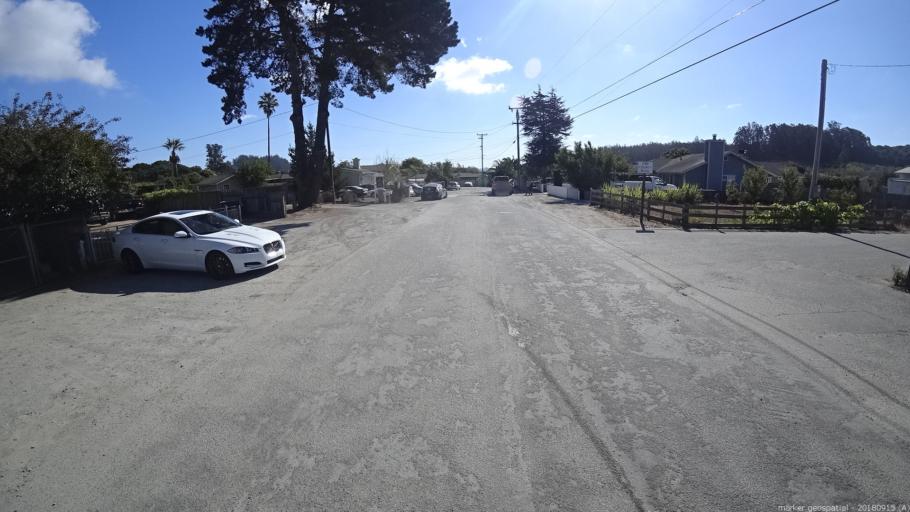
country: US
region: California
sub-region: Monterey County
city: Las Lomas
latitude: 36.8631
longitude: -121.7335
